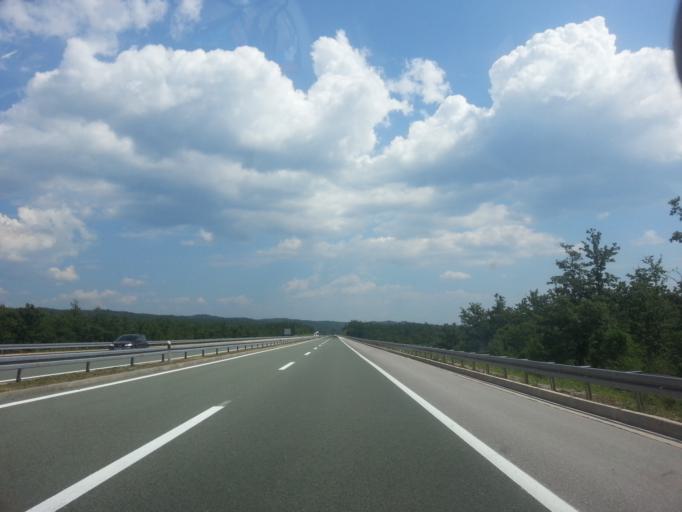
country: HR
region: Primorsko-Goranska
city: Matulji
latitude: 45.4337
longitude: 14.2831
